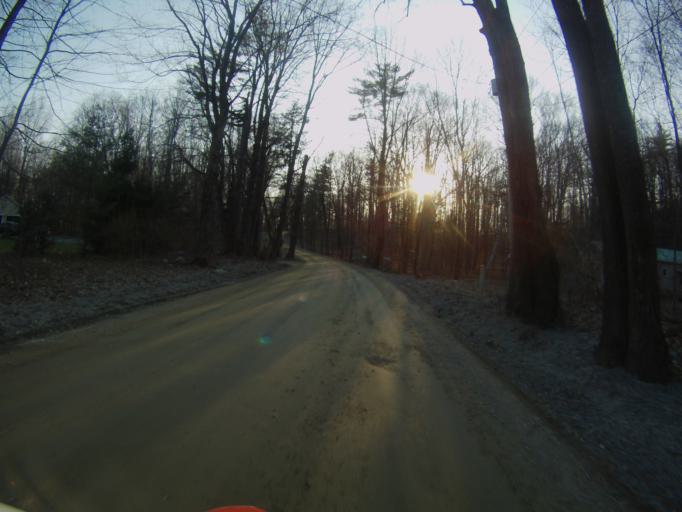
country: US
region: Vermont
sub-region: Addison County
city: Bristol
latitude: 44.0544
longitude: -73.0949
